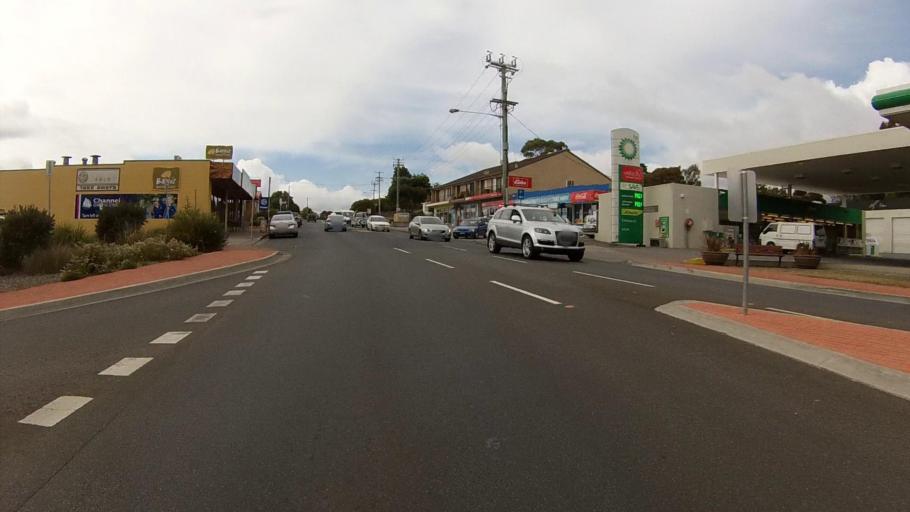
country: AU
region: Tasmania
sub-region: Kingborough
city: Margate
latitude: -43.0263
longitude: 147.2612
